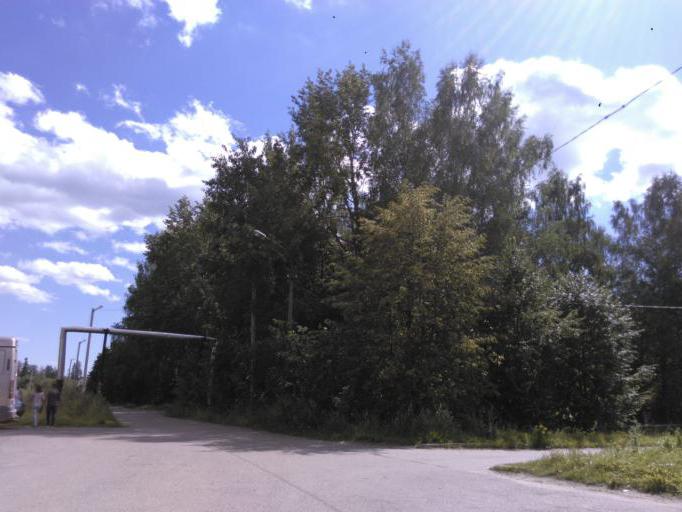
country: RU
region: Moskovskaya
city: Solnechnogorsk
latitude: 56.1409
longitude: 36.8944
